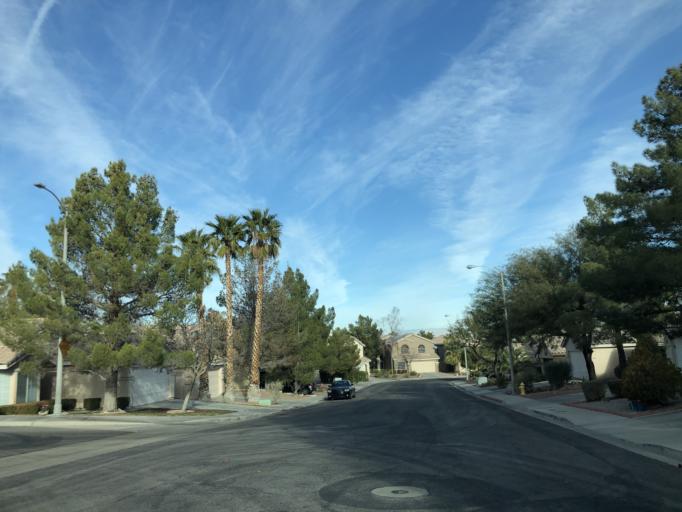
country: US
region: Nevada
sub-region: Clark County
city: Whitney
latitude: 36.0205
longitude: -115.0721
